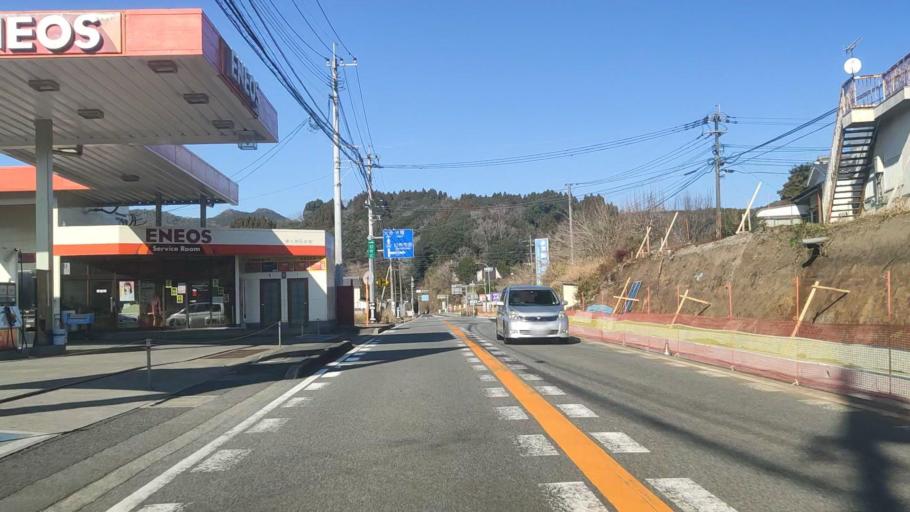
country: JP
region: Oita
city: Usuki
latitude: 33.0509
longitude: 131.6889
